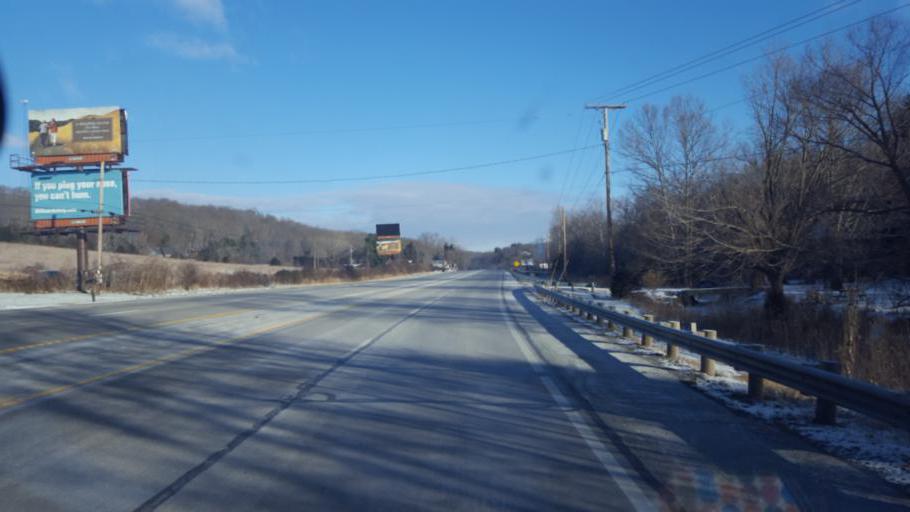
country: US
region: Ohio
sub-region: Ross County
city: Chillicothe
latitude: 39.2350
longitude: -82.9844
